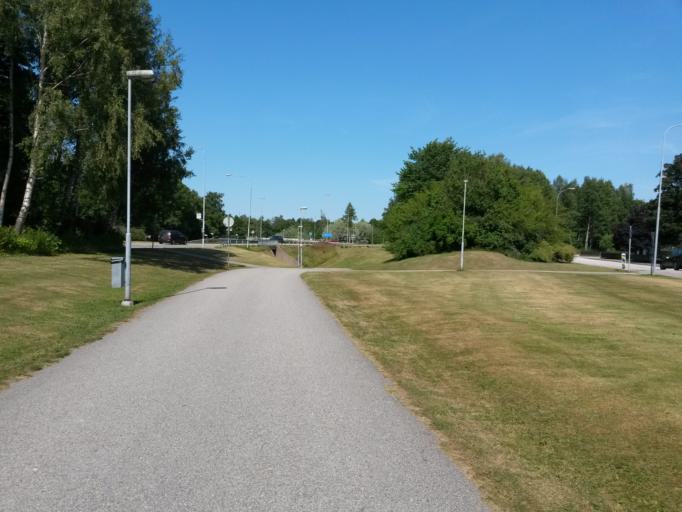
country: SE
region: Vaestra Goetaland
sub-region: Lidkopings Kommun
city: Lidkoping
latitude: 58.4899
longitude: 13.1448
